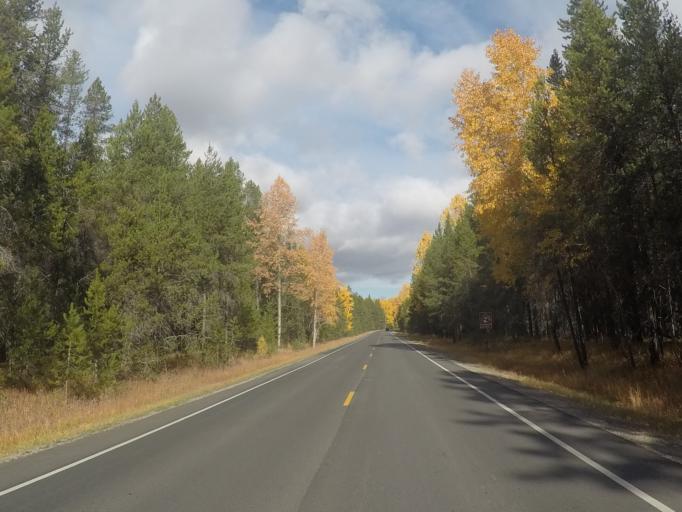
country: US
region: Montana
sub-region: Flathead County
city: Columbia Falls
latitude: 48.5144
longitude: -113.9884
